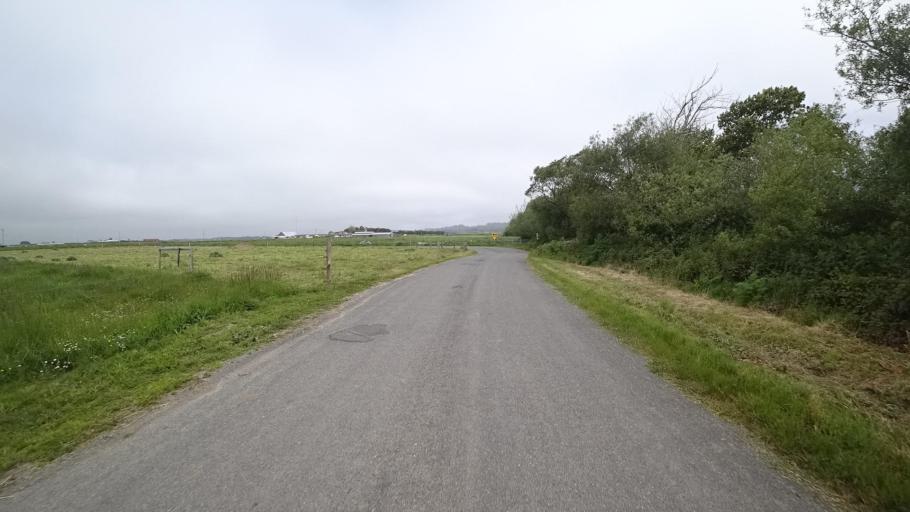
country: US
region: California
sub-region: Humboldt County
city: Fortuna
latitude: 40.5910
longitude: -124.1891
